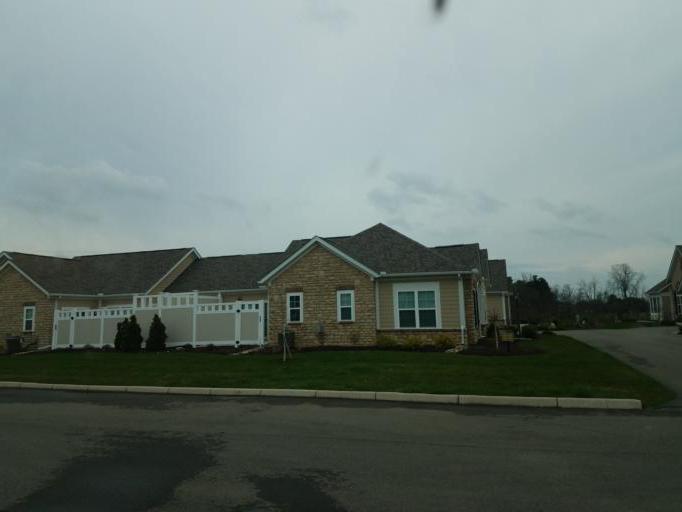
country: US
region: Ohio
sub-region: Richland County
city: Lexington
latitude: 40.7202
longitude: -82.5654
